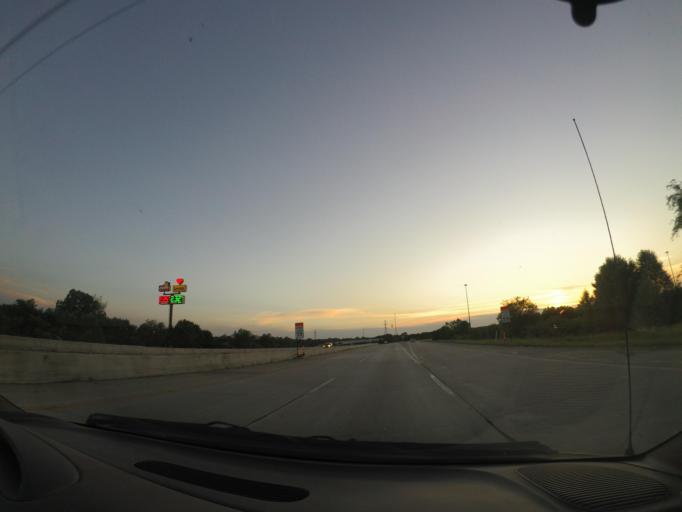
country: US
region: Indiana
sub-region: Elkhart County
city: Dunlap
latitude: 41.6669
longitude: -85.8881
